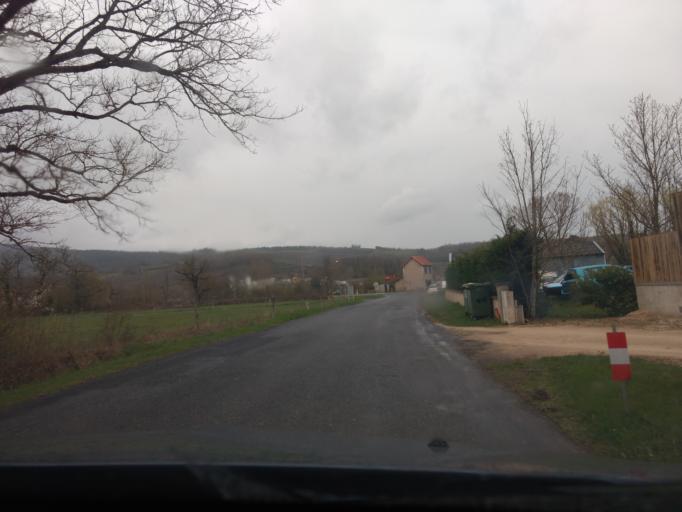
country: FR
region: Midi-Pyrenees
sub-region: Departement de l'Aveyron
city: La Loubiere
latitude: 44.3912
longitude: 2.6965
